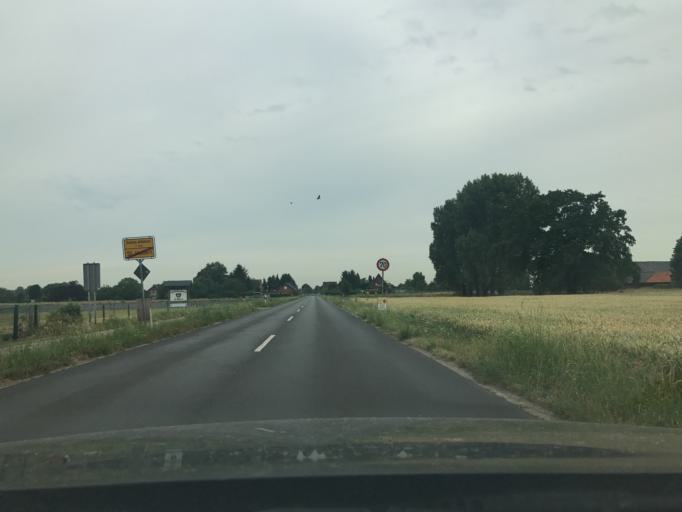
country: DE
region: North Rhine-Westphalia
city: Kempen
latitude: 51.3865
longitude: 6.4412
